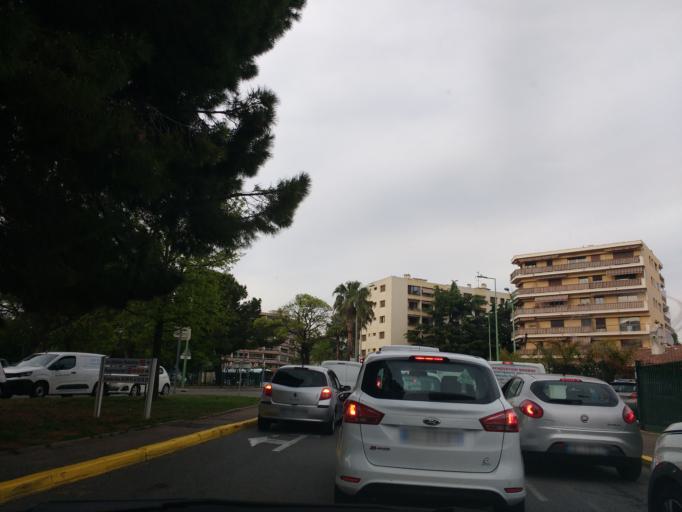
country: FR
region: Provence-Alpes-Cote d'Azur
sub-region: Departement des Alpes-Maritimes
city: Le Cannet
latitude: 43.5760
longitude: 6.9976
